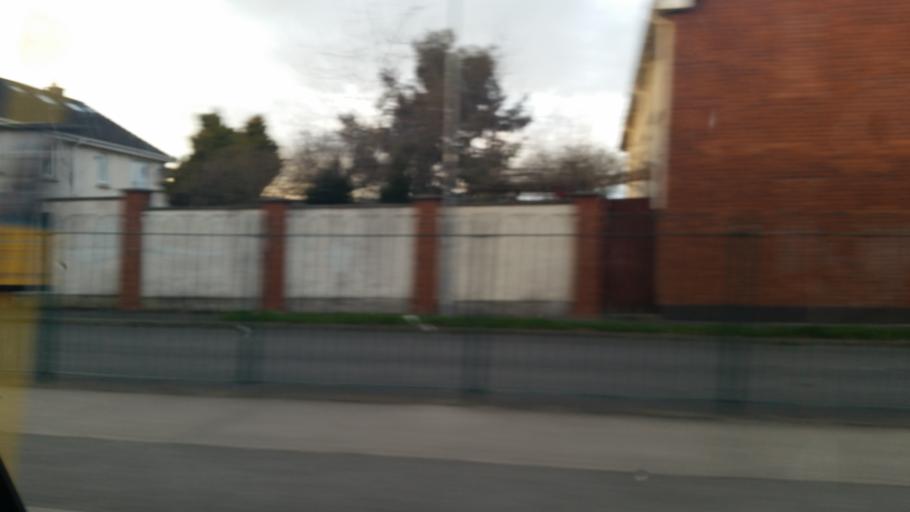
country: IE
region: Leinster
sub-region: Fingal County
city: Blanchardstown
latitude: 53.4045
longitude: -6.3920
